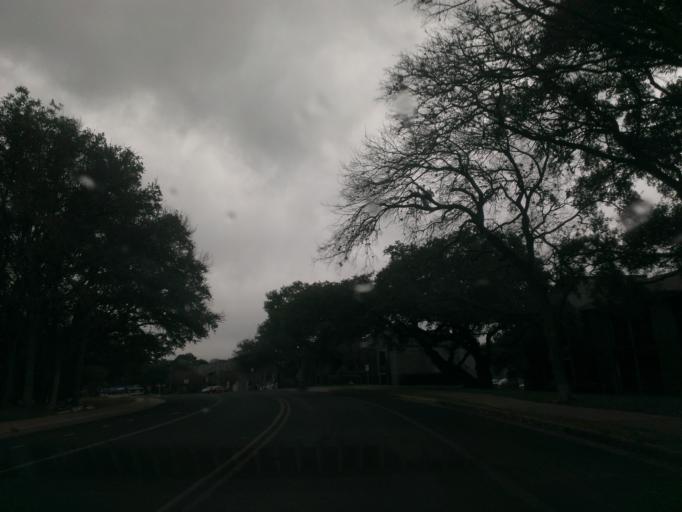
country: US
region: Texas
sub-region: Travis County
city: West Lake Hills
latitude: 30.3583
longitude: -97.7528
